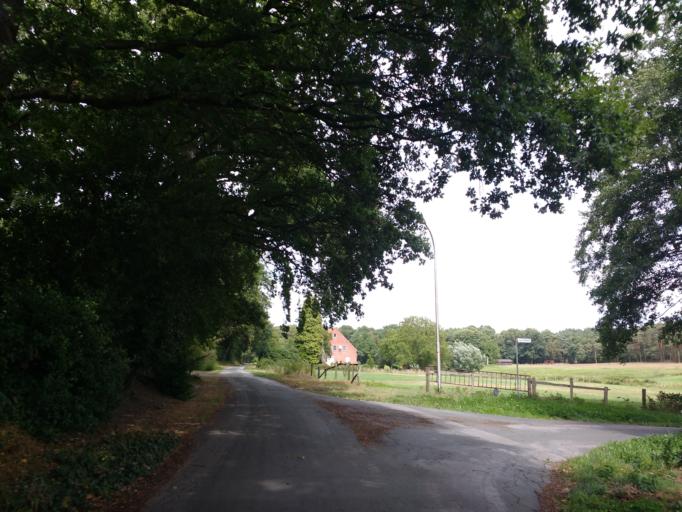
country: DE
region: Lower Saxony
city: Stolzenau
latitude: 52.4387
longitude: 9.0619
